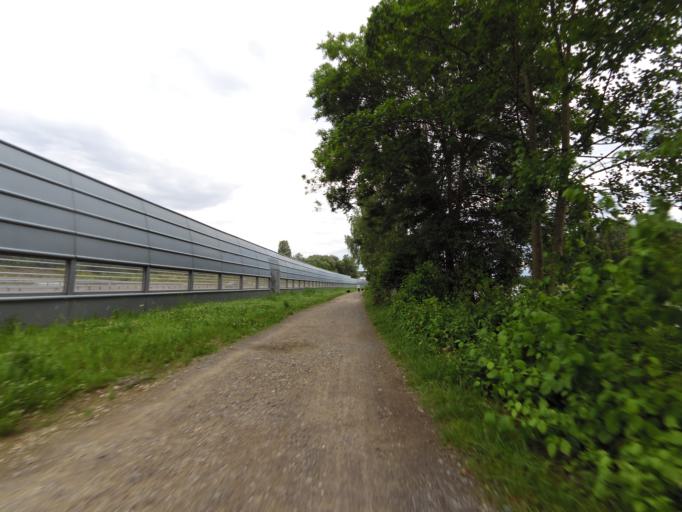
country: CH
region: Zurich
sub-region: Bezirk Dietikon
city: Unterengstringen
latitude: 47.4098
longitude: 8.4498
